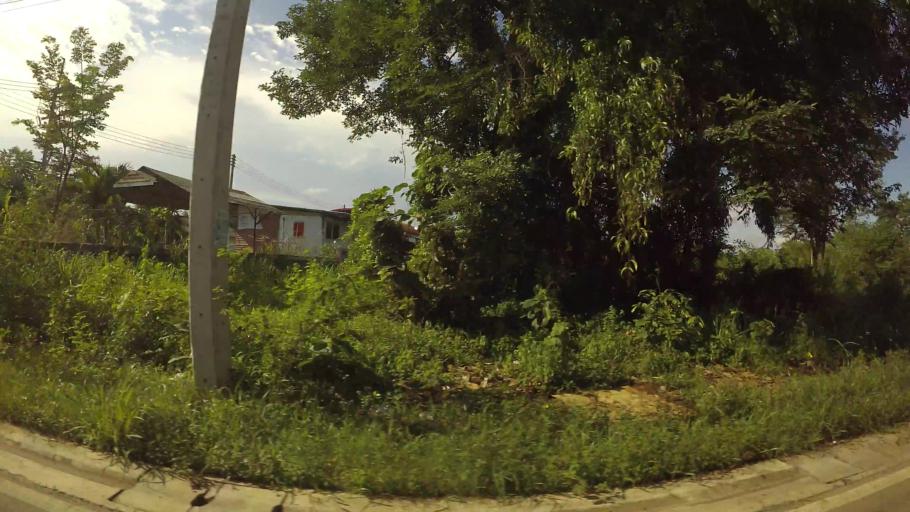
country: TH
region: Rayong
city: Rayong
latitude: 12.6704
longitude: 101.2971
